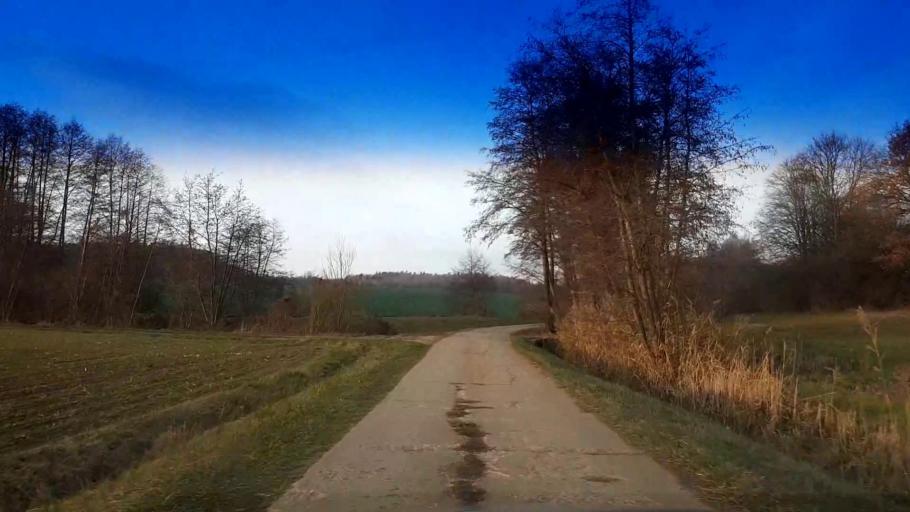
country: DE
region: Bavaria
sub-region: Upper Franconia
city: Schesslitz
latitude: 49.9774
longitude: 10.9853
